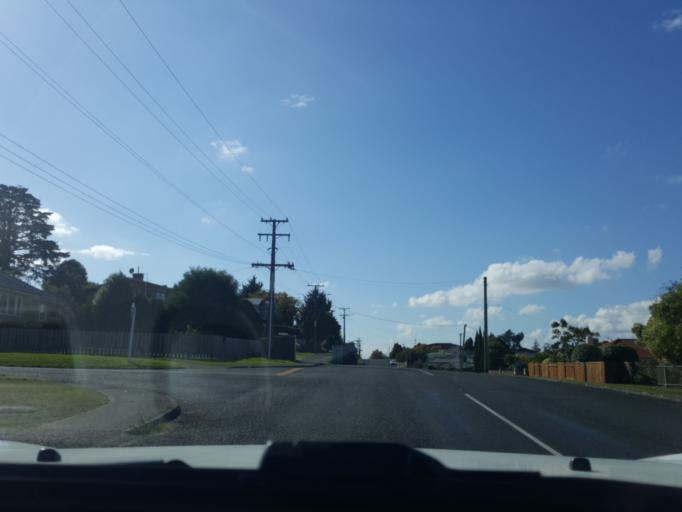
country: NZ
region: Waikato
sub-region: Waikato District
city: Ngaruawahia
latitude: -37.5460
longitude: 175.1686
